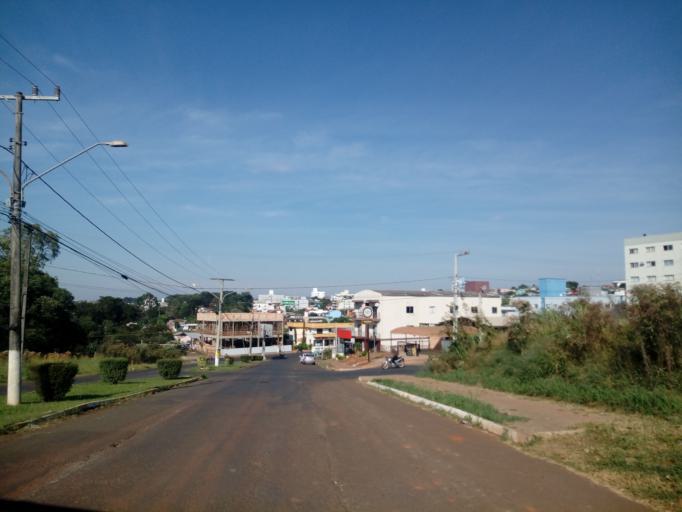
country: BR
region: Santa Catarina
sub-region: Chapeco
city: Chapeco
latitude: -27.0950
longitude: -52.6671
